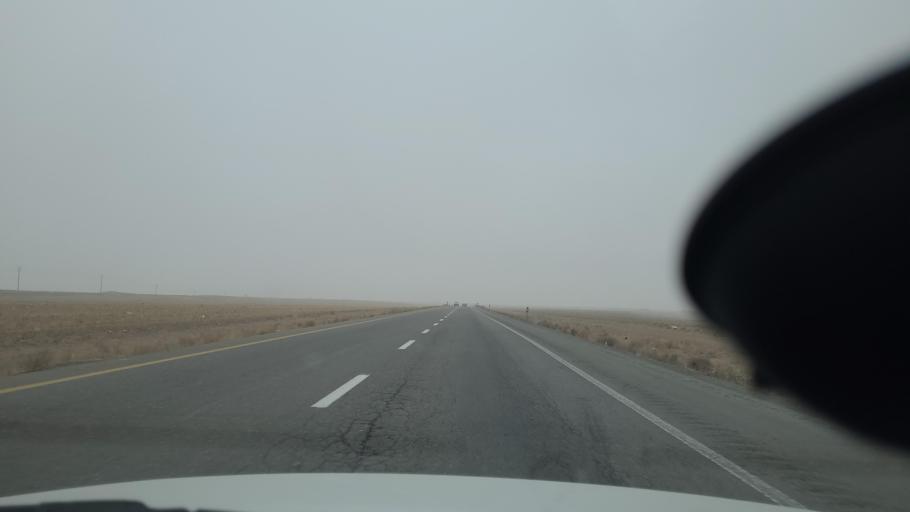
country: IR
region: Razavi Khorasan
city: Fariman
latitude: 35.8444
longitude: 59.7534
